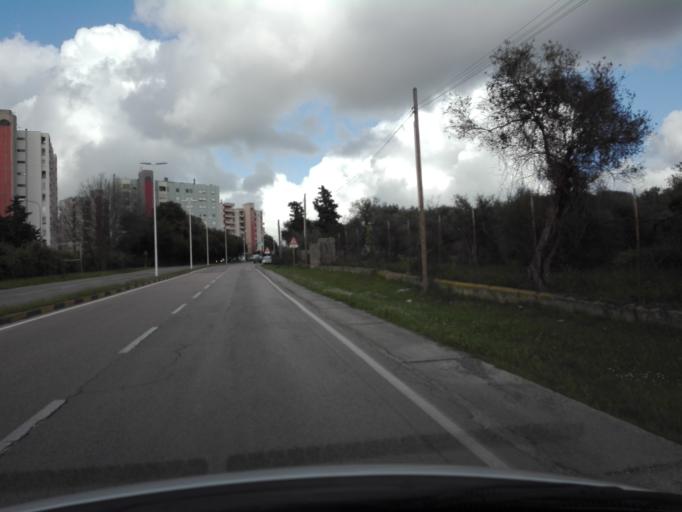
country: IT
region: Sardinia
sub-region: Provincia di Sassari
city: Sassari
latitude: 40.7108
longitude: 8.5775
